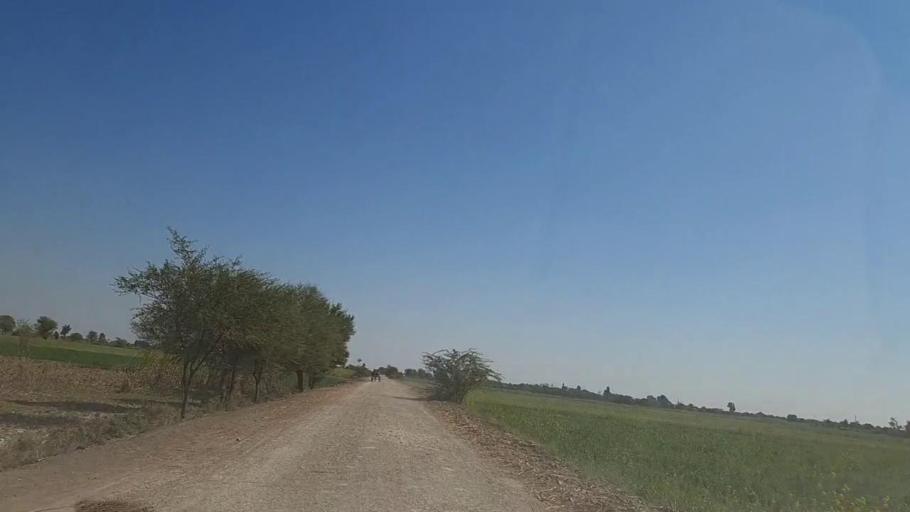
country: PK
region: Sindh
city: Digri
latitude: 25.1059
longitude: 69.1235
